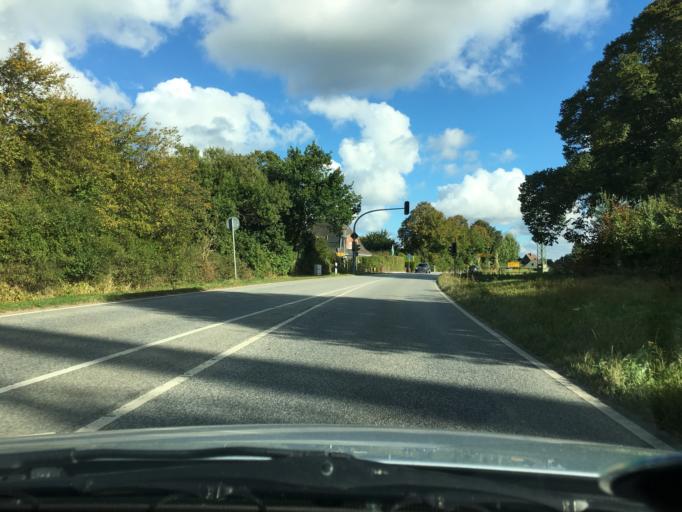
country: DE
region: Schleswig-Holstein
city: Krokau
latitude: 54.4070
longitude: 10.3367
